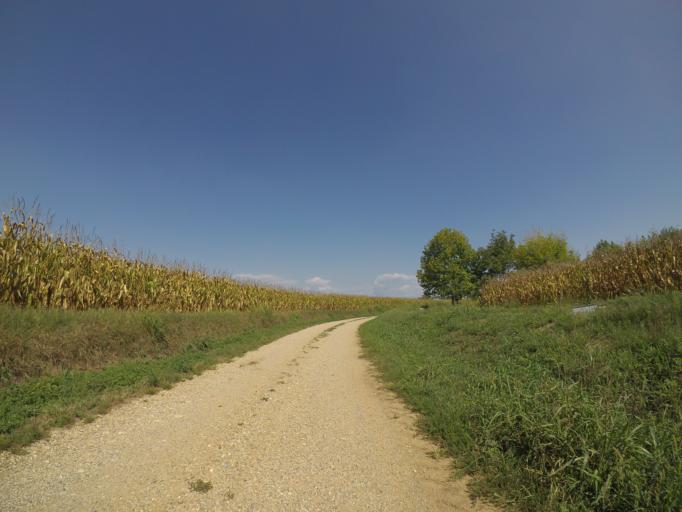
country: IT
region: Friuli Venezia Giulia
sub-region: Provincia di Udine
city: Bertiolo
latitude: 45.9406
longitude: 13.0757
